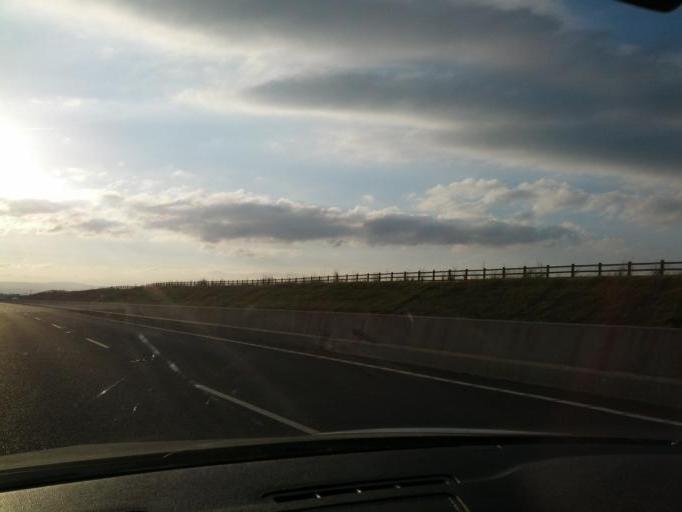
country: IE
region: Munster
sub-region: North Tipperary
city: Nenagh
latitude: 52.8633
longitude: -8.0971
